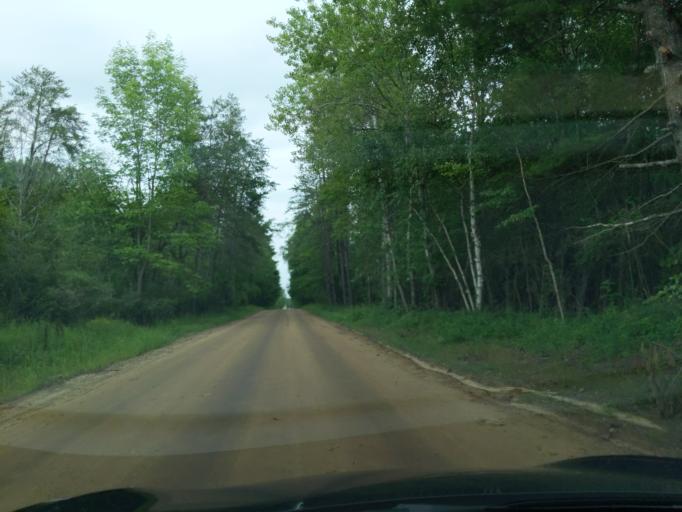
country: US
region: Michigan
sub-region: Clare County
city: Harrison
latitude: 43.9878
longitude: -85.0047
